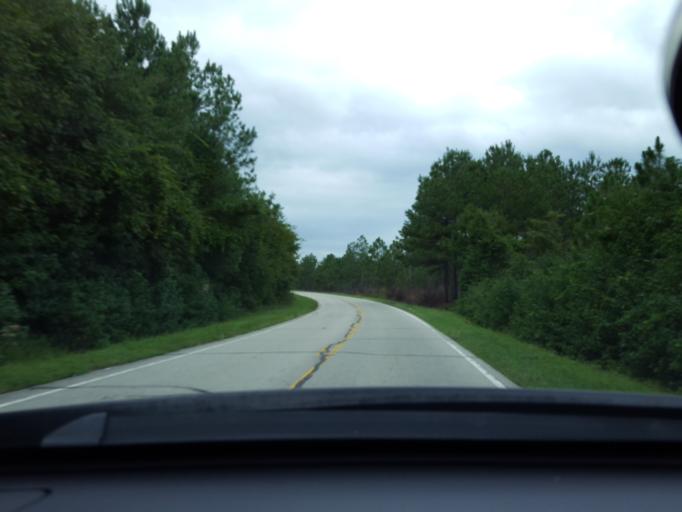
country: US
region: North Carolina
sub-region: Sampson County
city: Clinton
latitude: 34.8007
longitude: -78.2637
